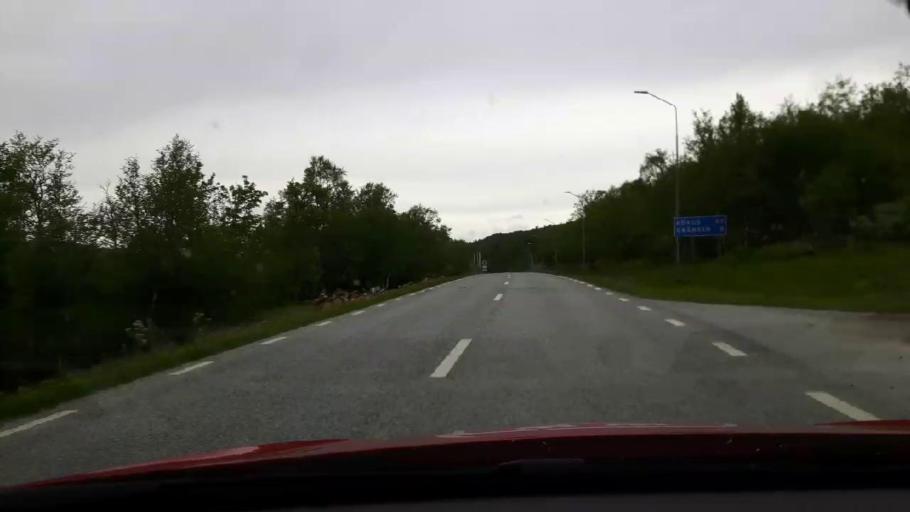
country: NO
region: Sor-Trondelag
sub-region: Tydal
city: Aas
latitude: 62.5967
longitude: 12.1823
